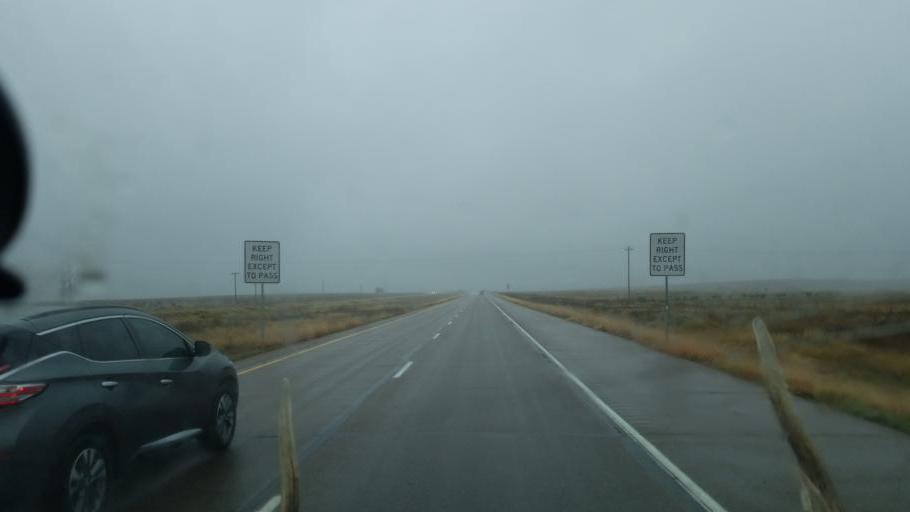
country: US
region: Colorado
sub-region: Pueblo County
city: Pueblo
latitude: 38.1353
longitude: -104.6649
